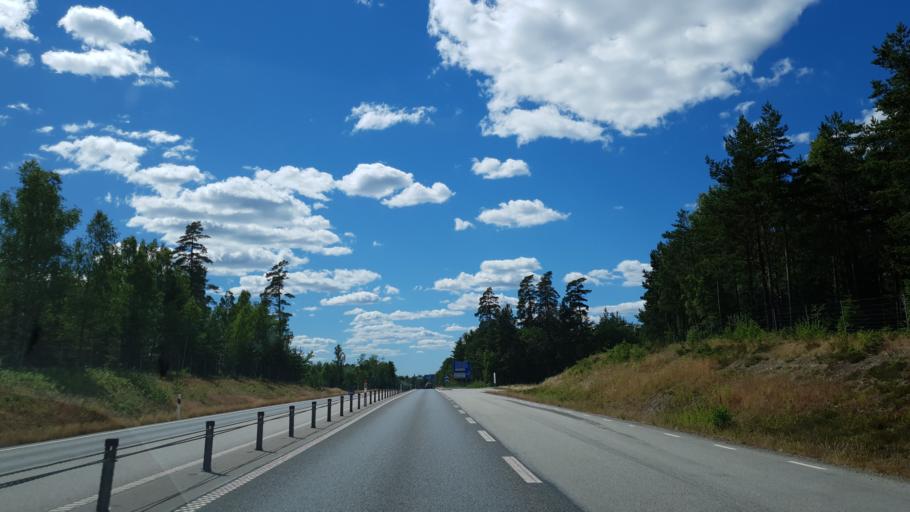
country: SE
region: Kronoberg
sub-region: Vaxjo Kommun
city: Vaexjoe
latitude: 56.8844
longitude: 14.8611
